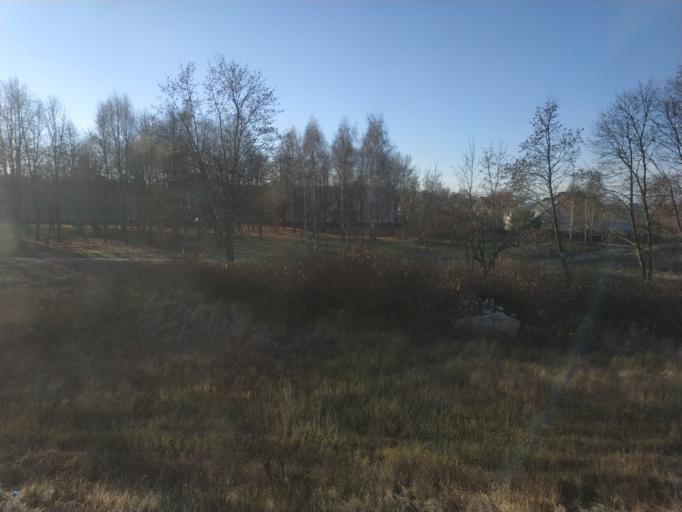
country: RU
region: Moskovskaya
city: Yam
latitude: 55.4903
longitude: 37.7295
